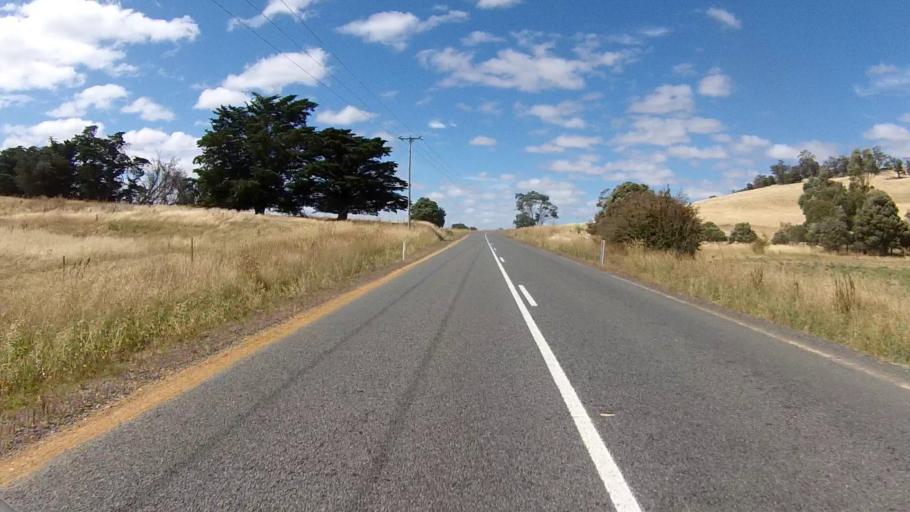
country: AU
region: Tasmania
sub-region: Brighton
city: Old Beach
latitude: -42.5971
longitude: 147.4146
